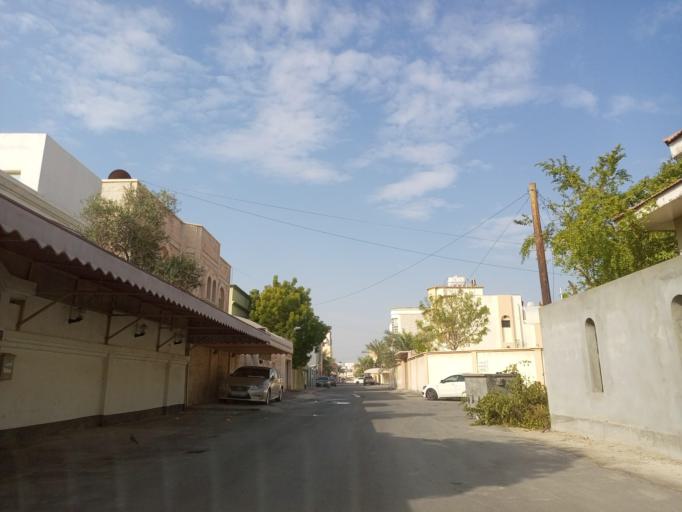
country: BH
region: Muharraq
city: Al Hadd
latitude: 26.2481
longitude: 50.6432
